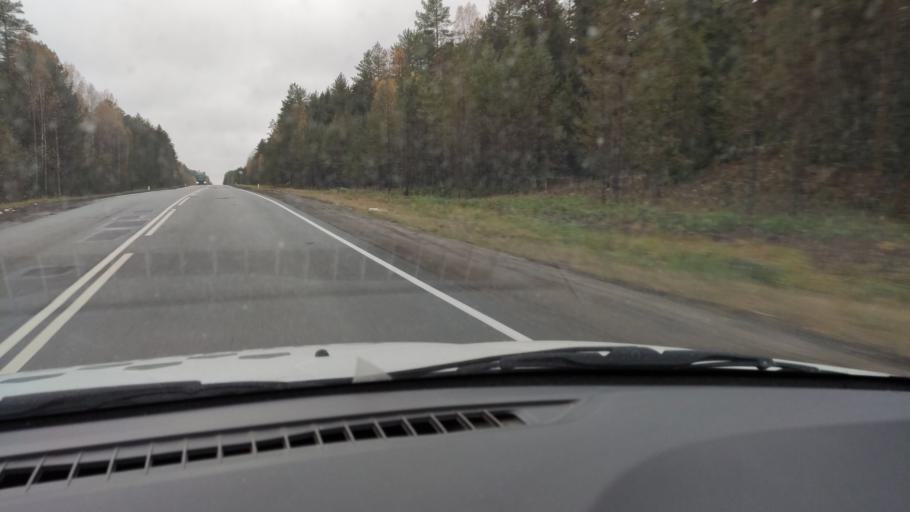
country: RU
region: Kirov
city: Dubrovka
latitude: 58.9083
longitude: 51.2449
